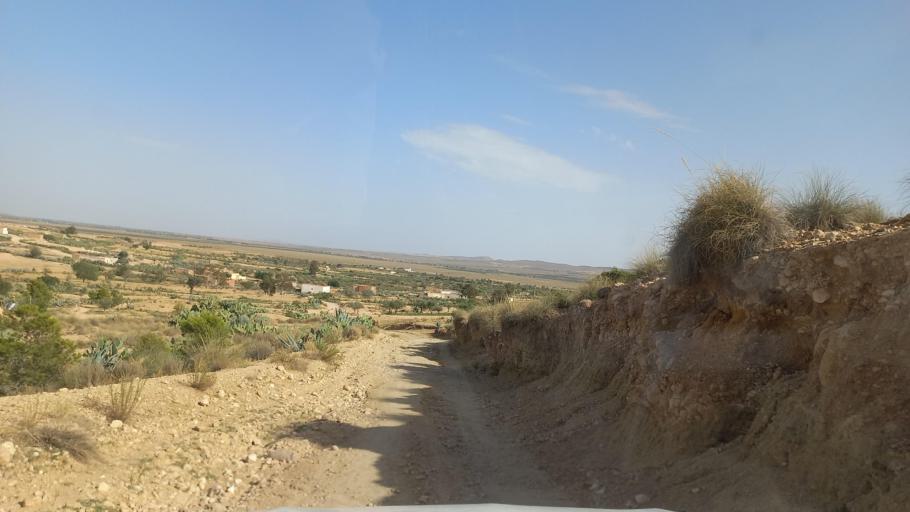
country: TN
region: Al Qasrayn
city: Kasserine
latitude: 35.2570
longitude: 8.9251
